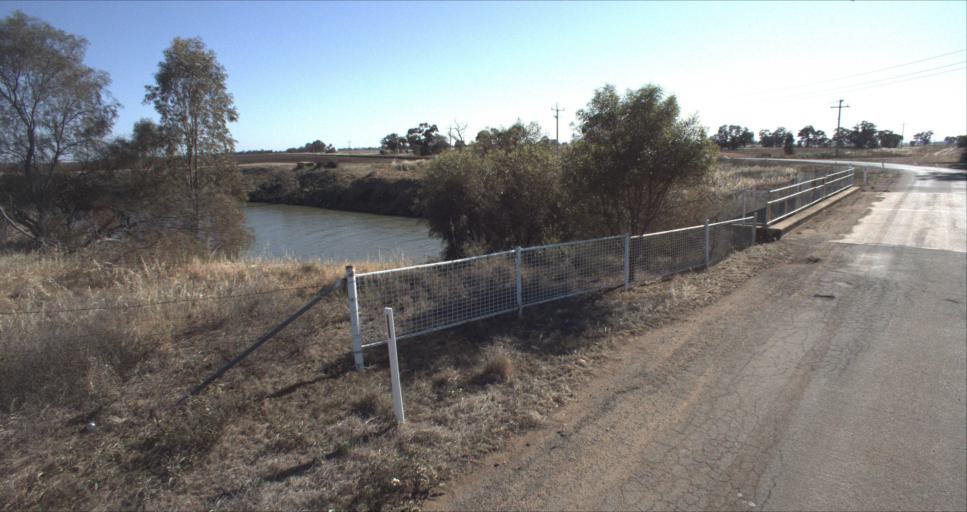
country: AU
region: New South Wales
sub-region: Leeton
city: Leeton
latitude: -34.6058
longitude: 146.2559
